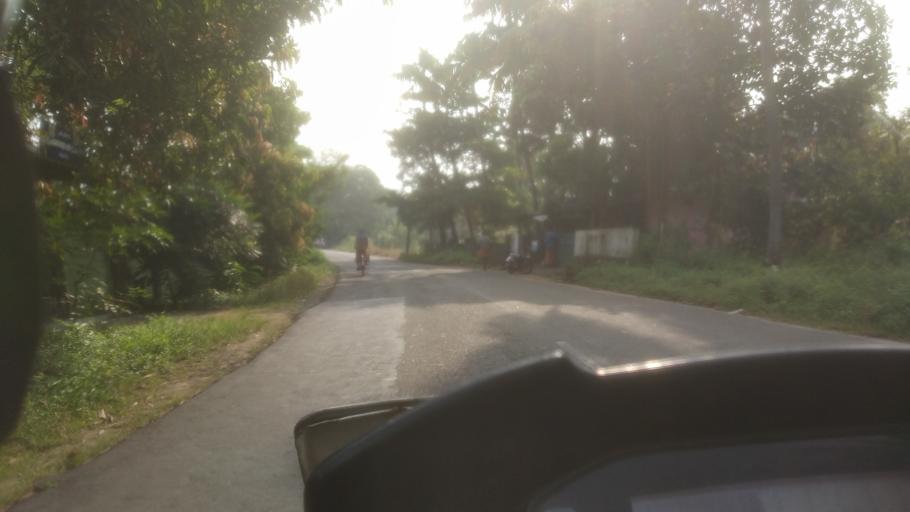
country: IN
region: Kerala
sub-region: Ernakulam
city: Angamali
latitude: 10.1617
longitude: 76.3788
